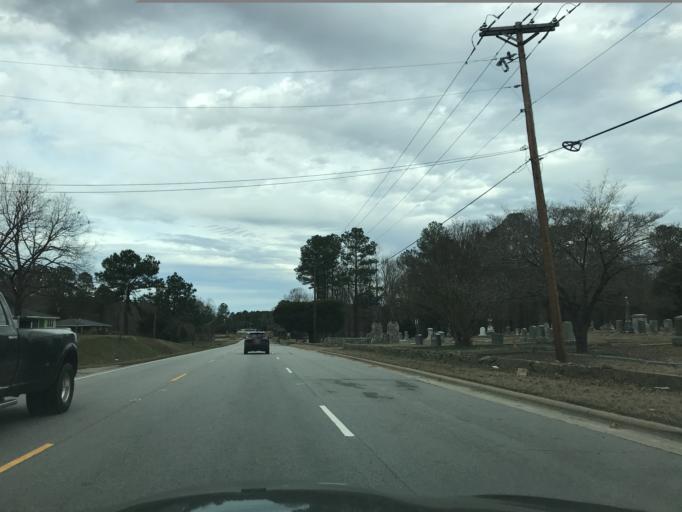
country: US
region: North Carolina
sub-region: Franklin County
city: Louisburg
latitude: 36.1221
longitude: -78.2946
